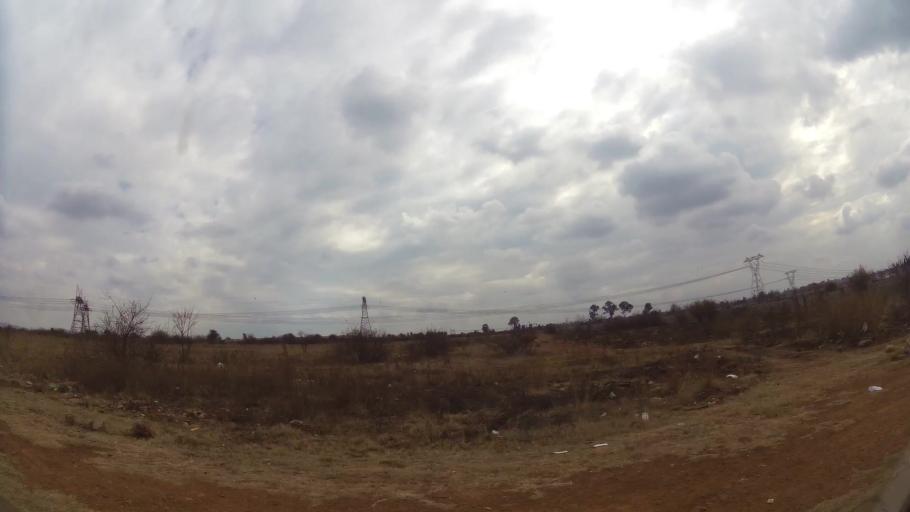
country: ZA
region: Gauteng
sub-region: Ekurhuleni Metropolitan Municipality
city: Germiston
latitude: -26.3792
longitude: 28.1127
